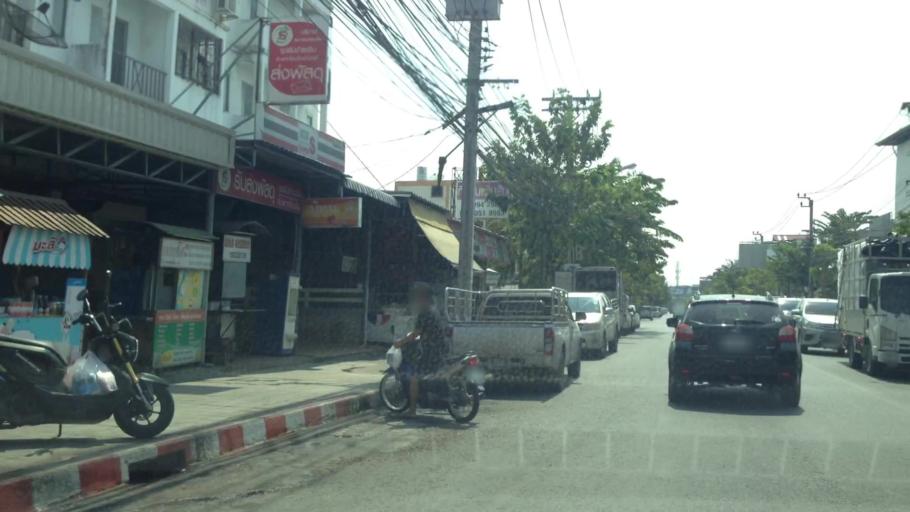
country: TH
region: Bangkok
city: Sai Mai
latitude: 13.9003
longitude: 100.6379
